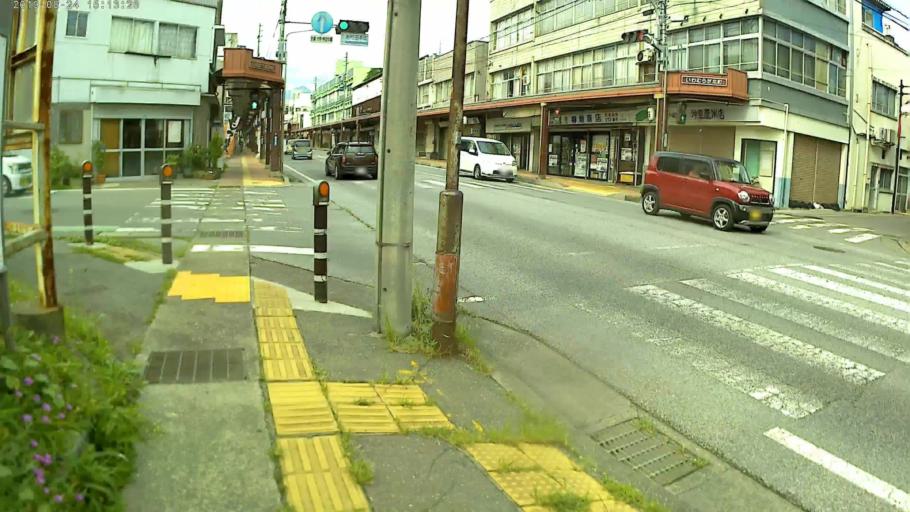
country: JP
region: Nagano
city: Saku
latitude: 36.2720
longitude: 138.4783
